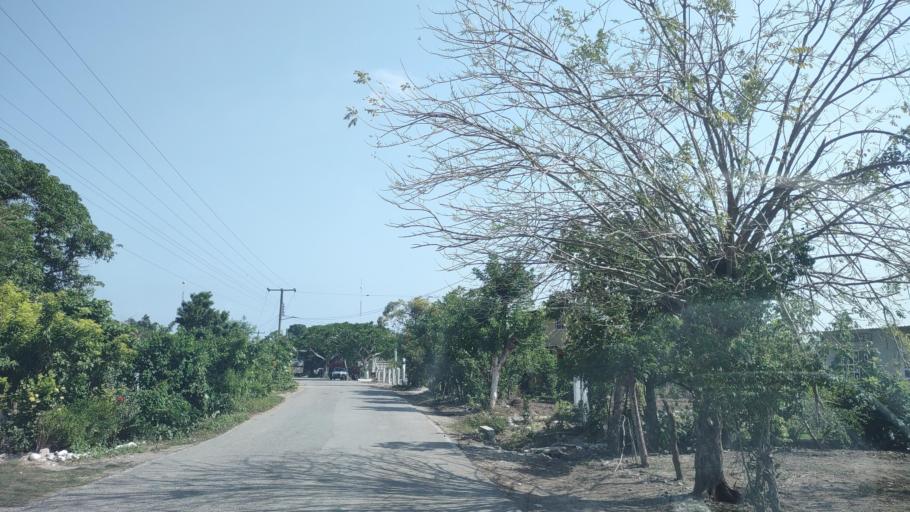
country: MX
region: Puebla
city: Espinal
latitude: 20.2545
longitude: -97.3313
